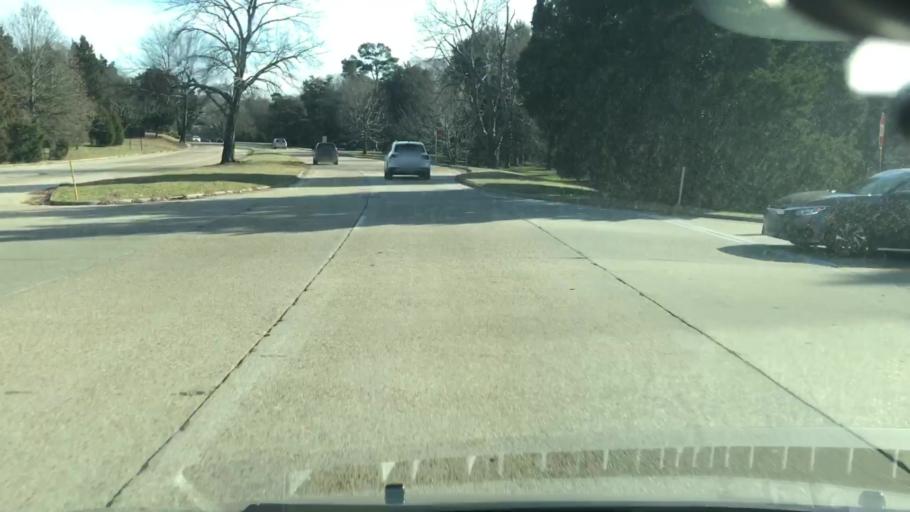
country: US
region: Virginia
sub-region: Fairfax County
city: Fort Hunt
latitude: 38.7324
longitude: -77.0477
